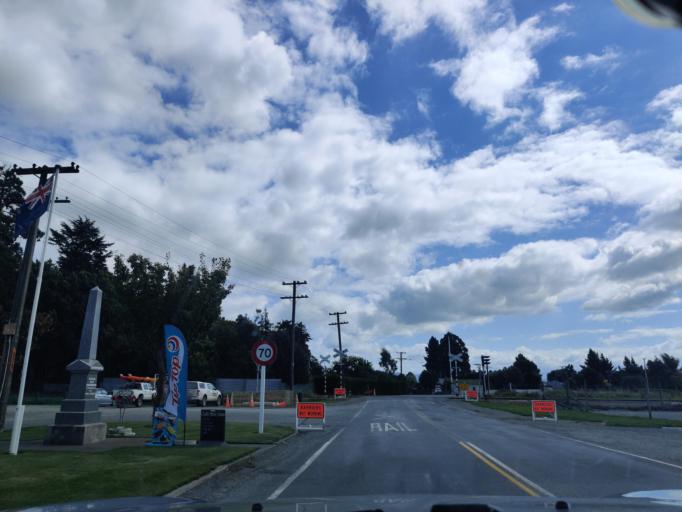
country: NZ
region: Canterbury
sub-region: Timaru District
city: Pleasant Point
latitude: -44.1373
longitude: 171.2977
